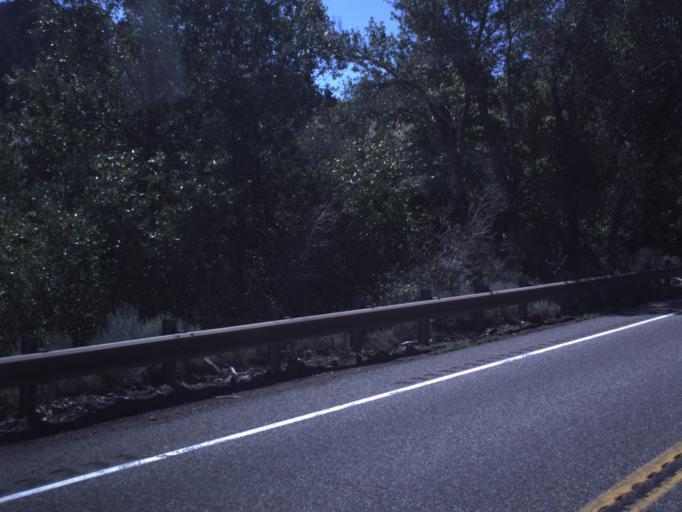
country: US
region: Utah
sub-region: Sevier County
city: Monroe
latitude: 38.5574
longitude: -112.2719
